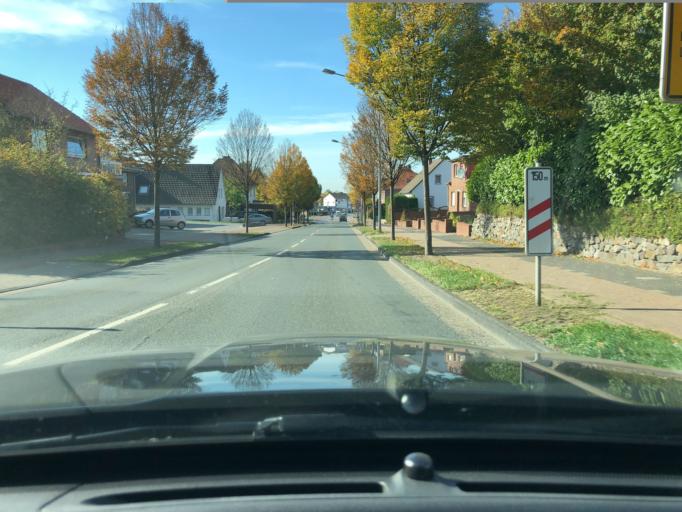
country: DE
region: North Rhine-Westphalia
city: Lengerich
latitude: 52.1867
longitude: 7.8662
